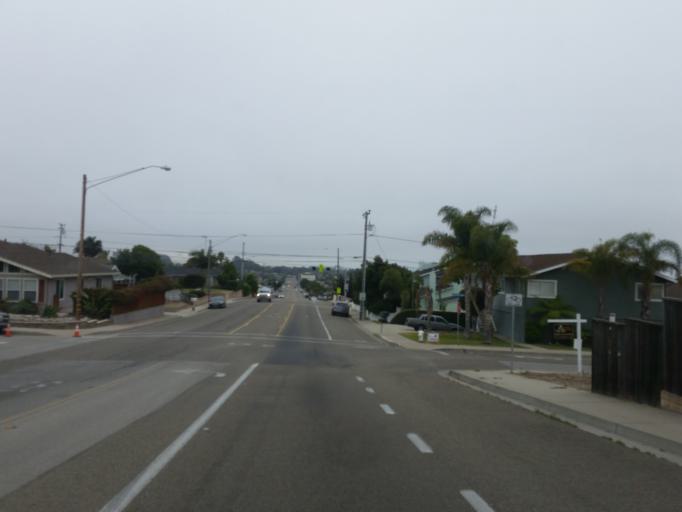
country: US
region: California
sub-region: San Luis Obispo County
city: Grover Beach
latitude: 35.1295
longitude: -120.6259
